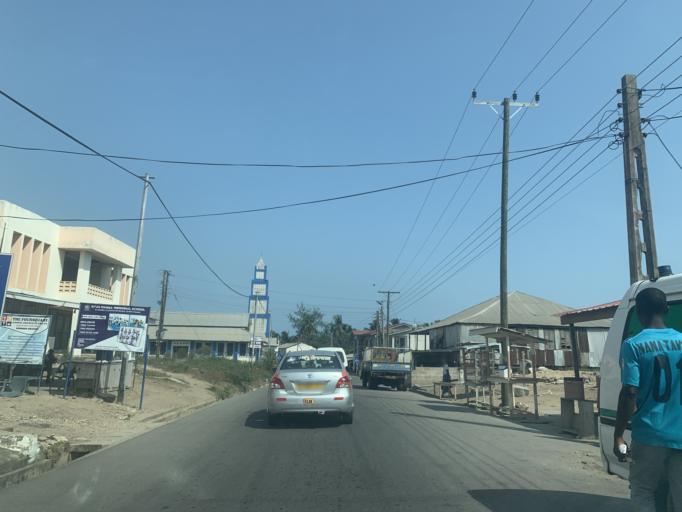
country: GH
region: Central
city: Winneba
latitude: 5.3440
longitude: -0.6275
